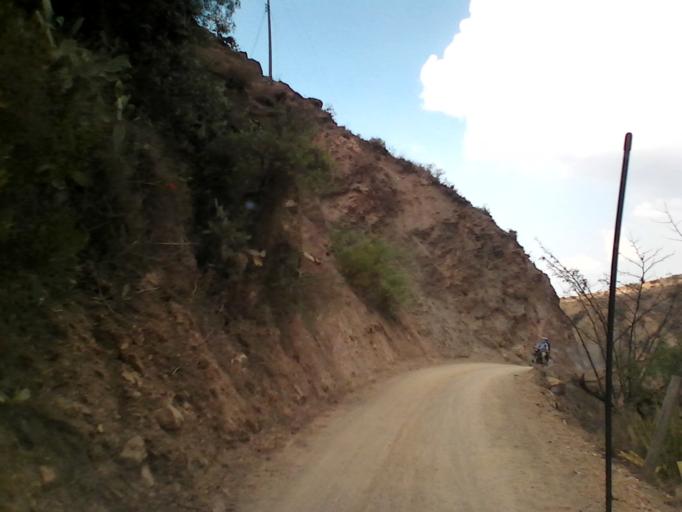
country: CO
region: Boyaca
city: Sachica
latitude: 5.5584
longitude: -73.5324
